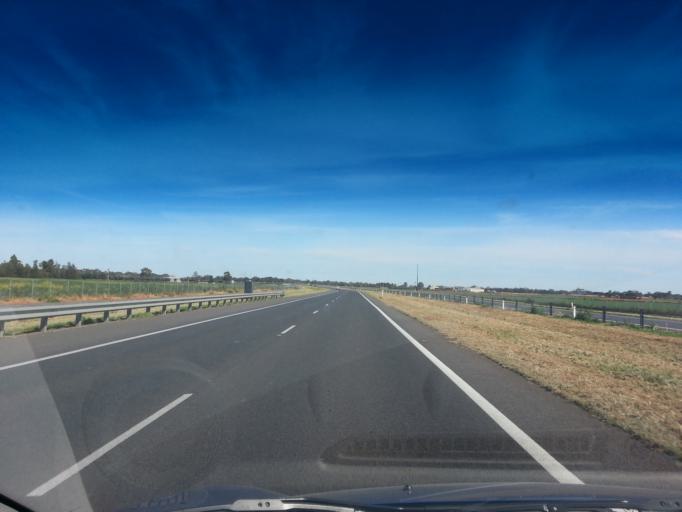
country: AU
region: South Australia
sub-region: Gawler
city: Gawler
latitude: -34.6064
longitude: 138.6949
